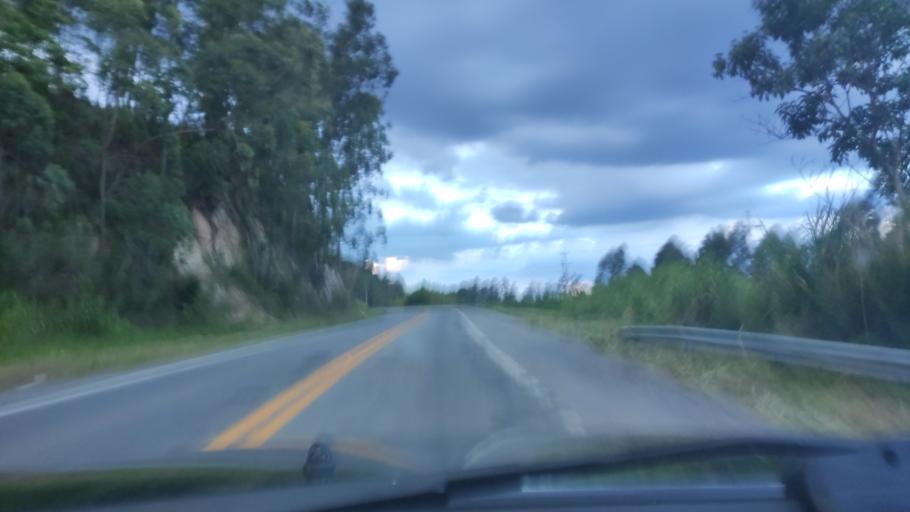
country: BR
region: Sao Paulo
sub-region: Braganca Paulista
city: Braganca Paulista
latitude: -22.8268
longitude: -46.5573
